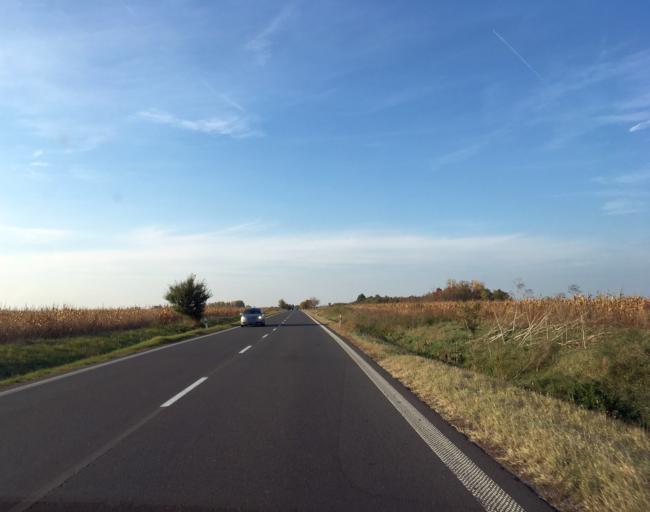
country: SK
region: Nitriansky
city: Surany
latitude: 48.0686
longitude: 18.0938
